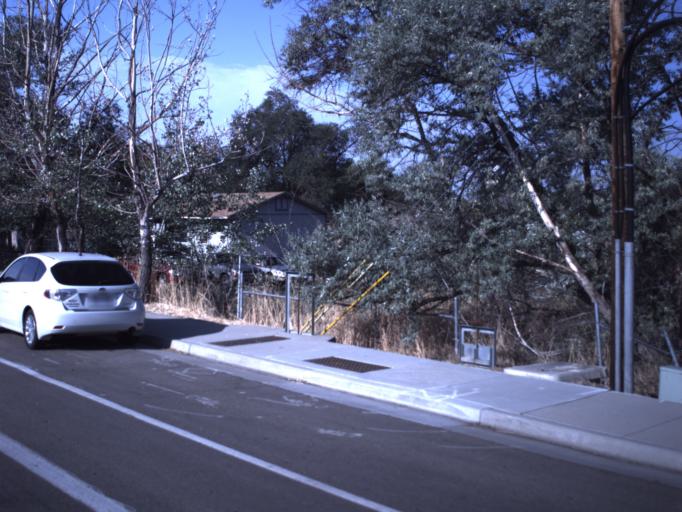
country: US
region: Utah
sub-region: Utah County
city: Cedar Hills
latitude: 40.4236
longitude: -111.7862
